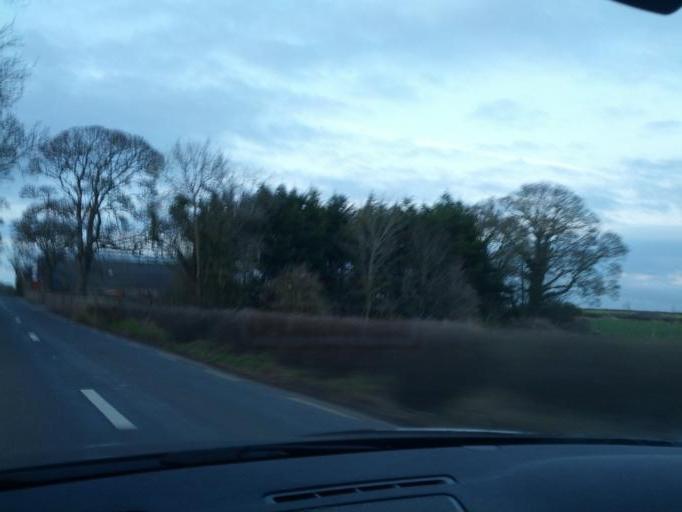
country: IE
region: Connaught
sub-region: County Galway
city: Portumna
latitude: 53.0335
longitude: -8.1178
